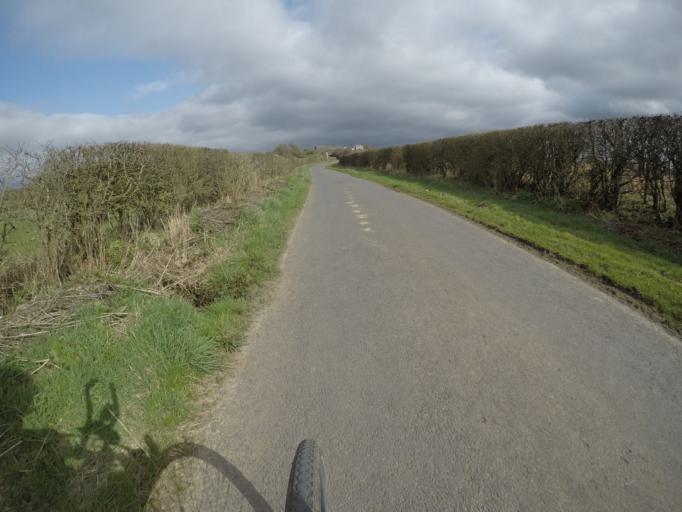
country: GB
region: Scotland
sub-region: North Ayrshire
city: Springside
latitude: 55.6466
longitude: -4.6205
